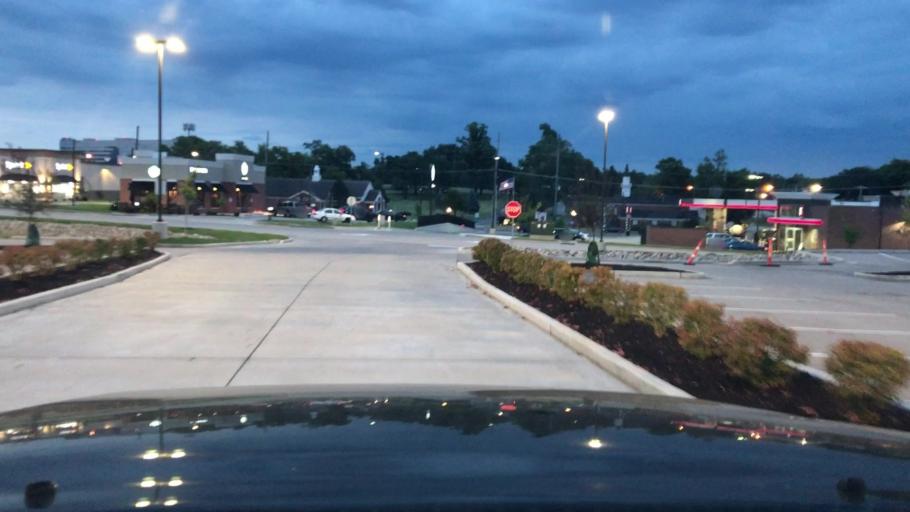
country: US
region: Missouri
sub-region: Saint Louis County
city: Saint Ann
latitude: 38.7355
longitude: -90.3986
